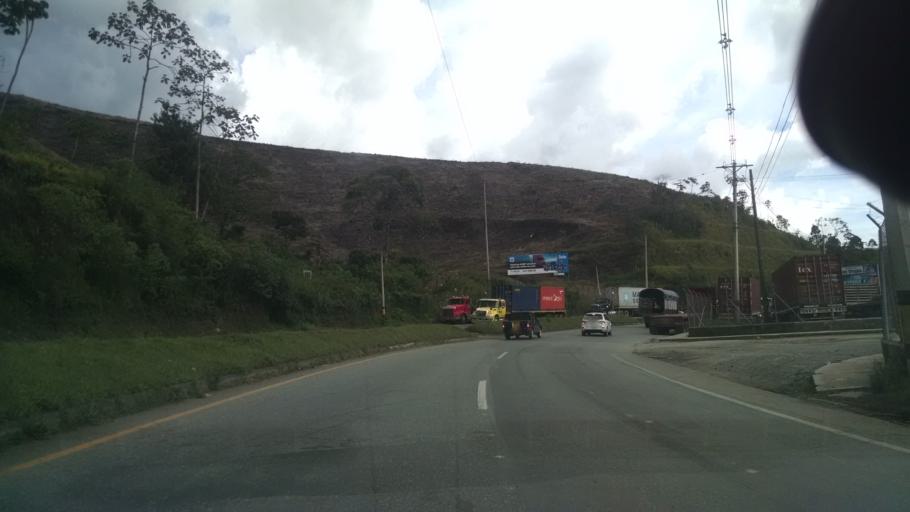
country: CO
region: Antioquia
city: Caldas
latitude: 6.0814
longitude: -75.6305
